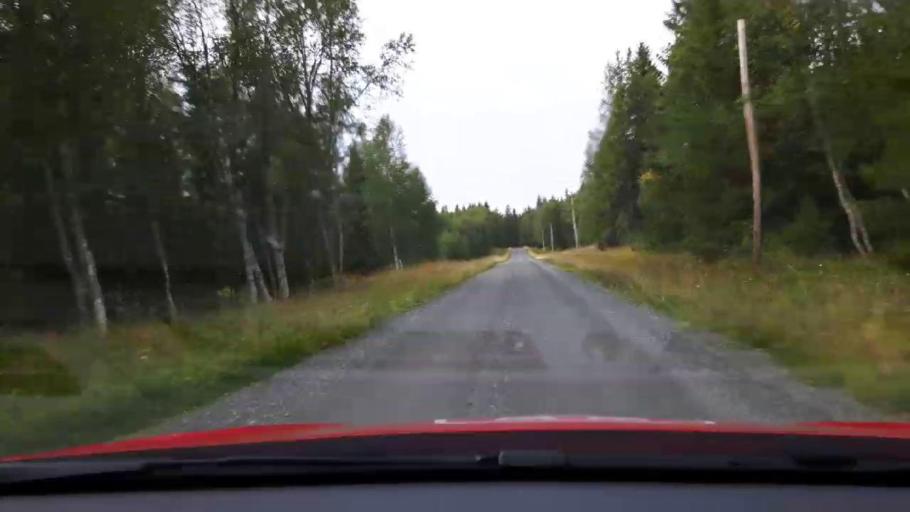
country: SE
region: Jaemtland
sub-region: Are Kommun
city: Are
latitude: 63.7713
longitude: 13.0851
